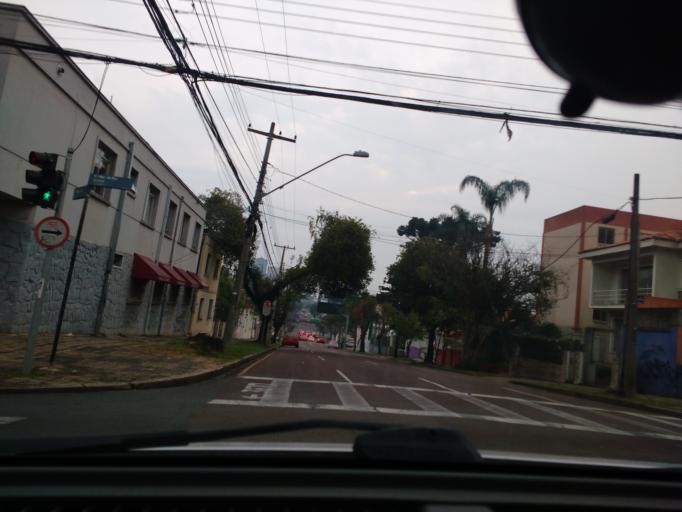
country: BR
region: Parana
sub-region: Curitiba
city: Curitiba
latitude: -25.4253
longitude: -49.2834
